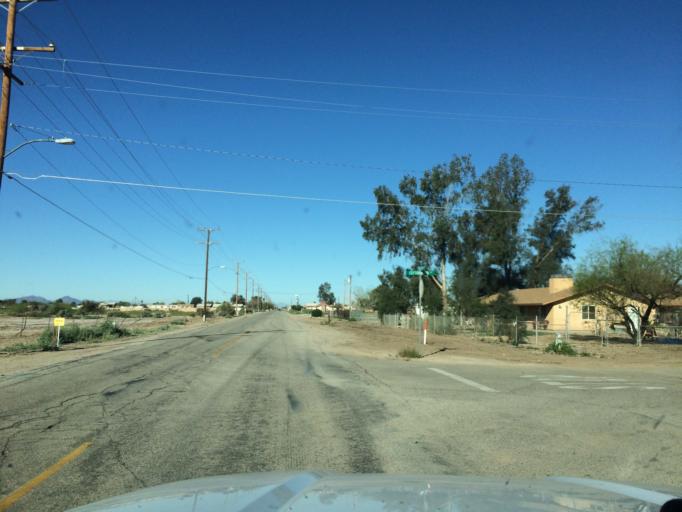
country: US
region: California
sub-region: Riverside County
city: Blythe
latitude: 33.6035
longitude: -114.5761
